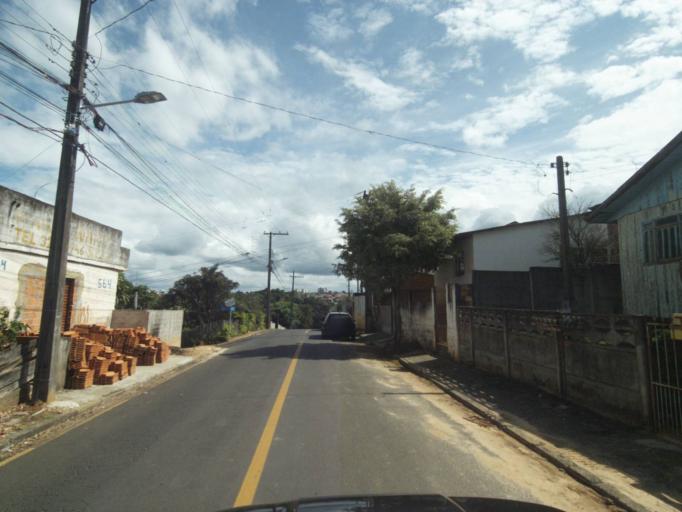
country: BR
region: Parana
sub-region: Telemaco Borba
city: Telemaco Borba
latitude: -24.3180
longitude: -50.6254
